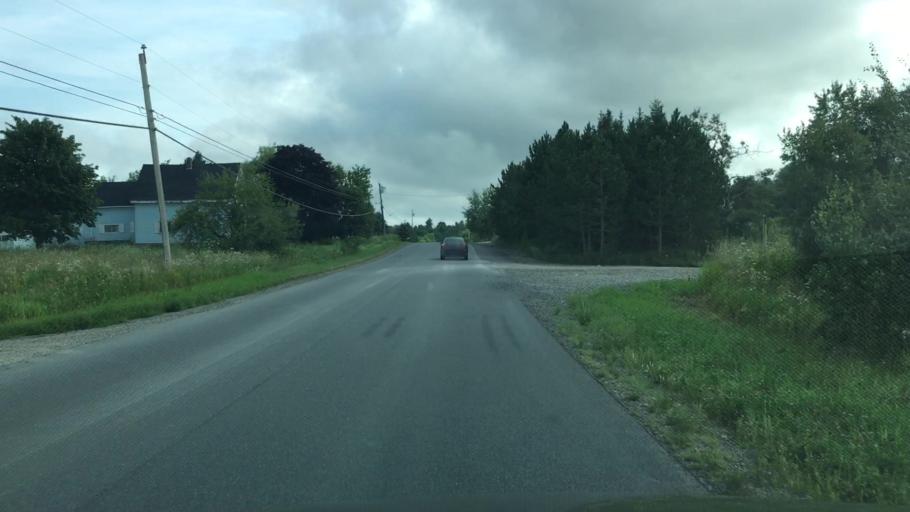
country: US
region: Maine
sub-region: Waldo County
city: Winterport
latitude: 44.6717
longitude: -68.8685
